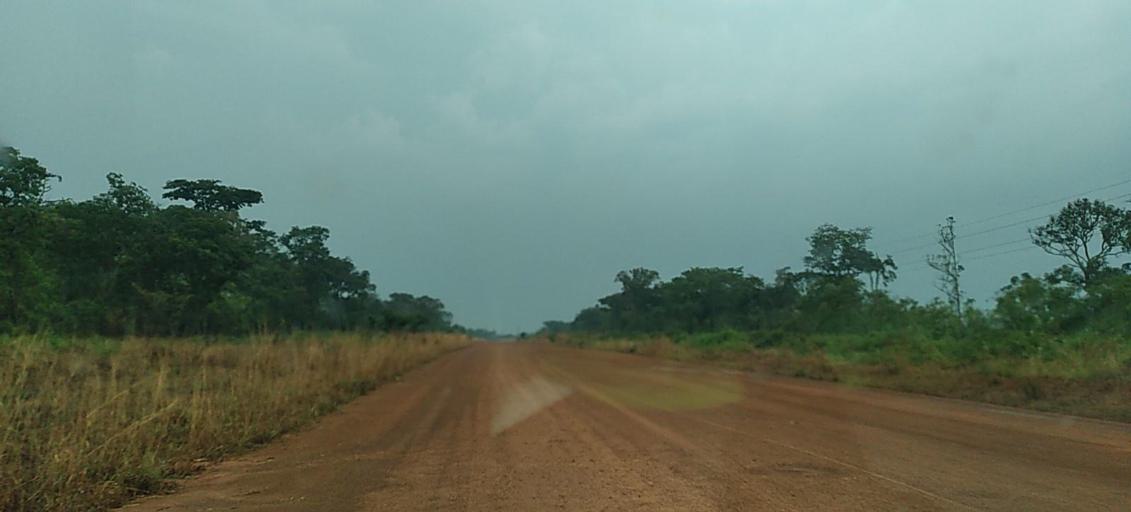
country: ZM
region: North-Western
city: Mwinilunga
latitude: -11.6097
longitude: 24.3976
